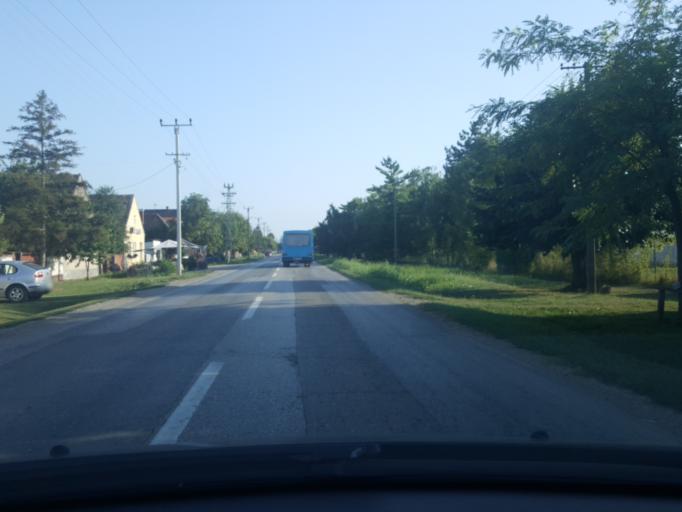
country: RS
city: Hrtkovci
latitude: 44.8857
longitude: 19.7636
